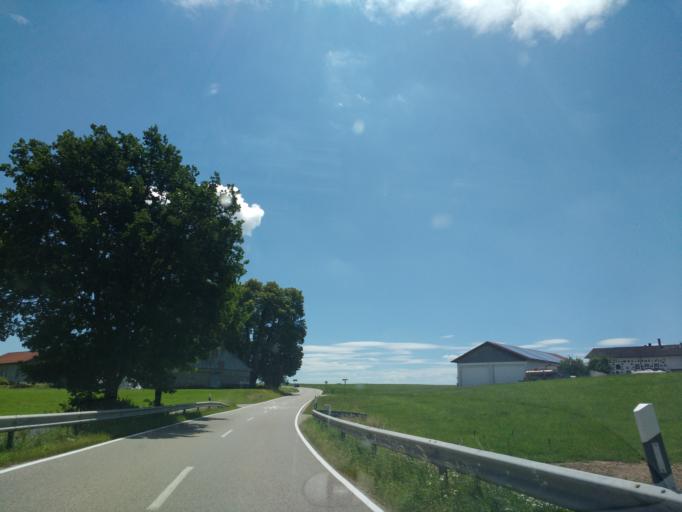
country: DE
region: Bavaria
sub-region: Upper Bavaria
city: Taufkirchen
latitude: 48.1339
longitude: 12.4849
